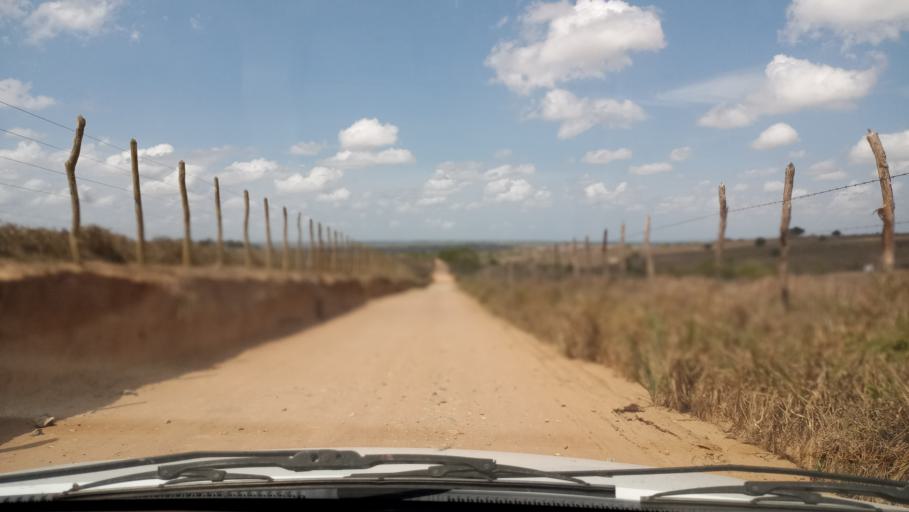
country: BR
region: Rio Grande do Norte
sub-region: Pedro Velho
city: Pedro Velho
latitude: -6.3463
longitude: -35.3297
